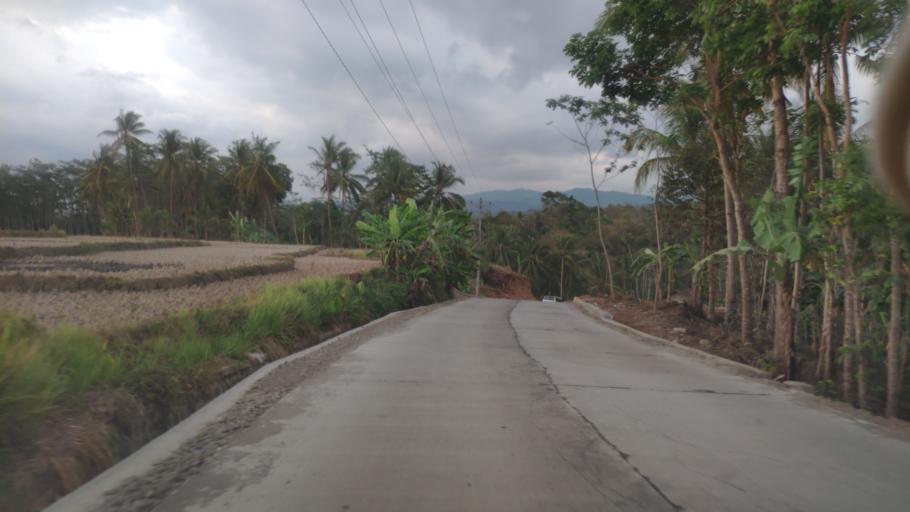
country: ID
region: Central Java
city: Wonosobo
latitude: -7.3747
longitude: 109.6638
